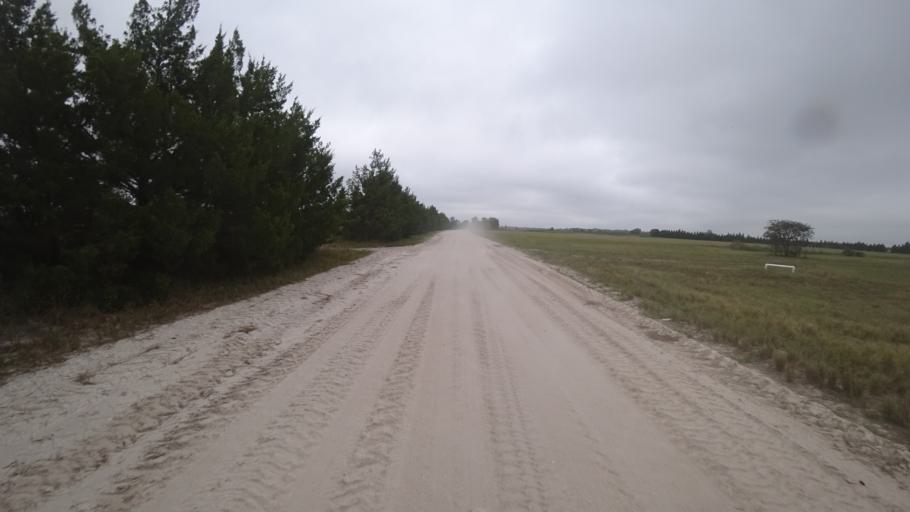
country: US
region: Florida
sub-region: Sarasota County
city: Warm Mineral Springs
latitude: 27.2981
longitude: -82.1345
